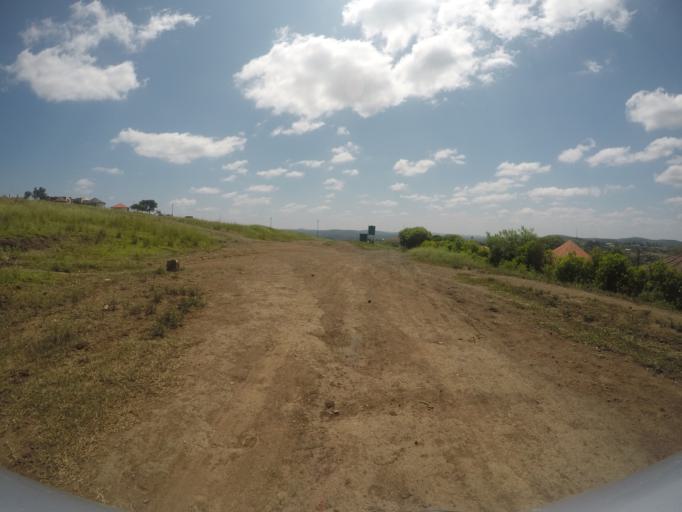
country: ZA
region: KwaZulu-Natal
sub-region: uThungulu District Municipality
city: Empangeni
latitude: -28.6083
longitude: 31.7323
